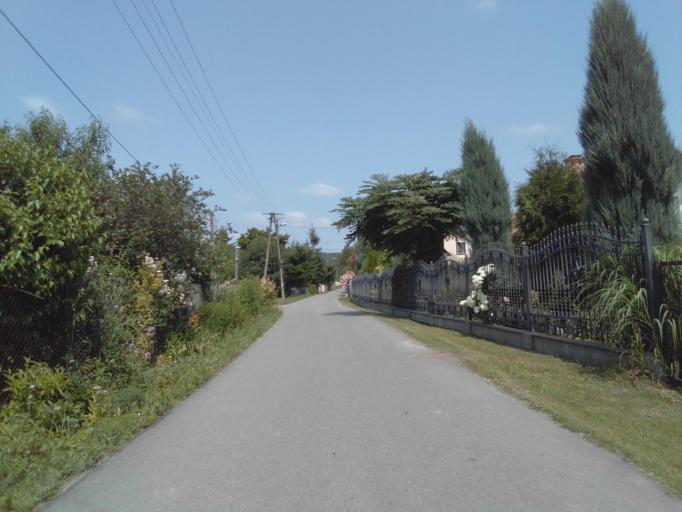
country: PL
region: Subcarpathian Voivodeship
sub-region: Powiat strzyzowski
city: Czudec
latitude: 49.9414
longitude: 21.8288
